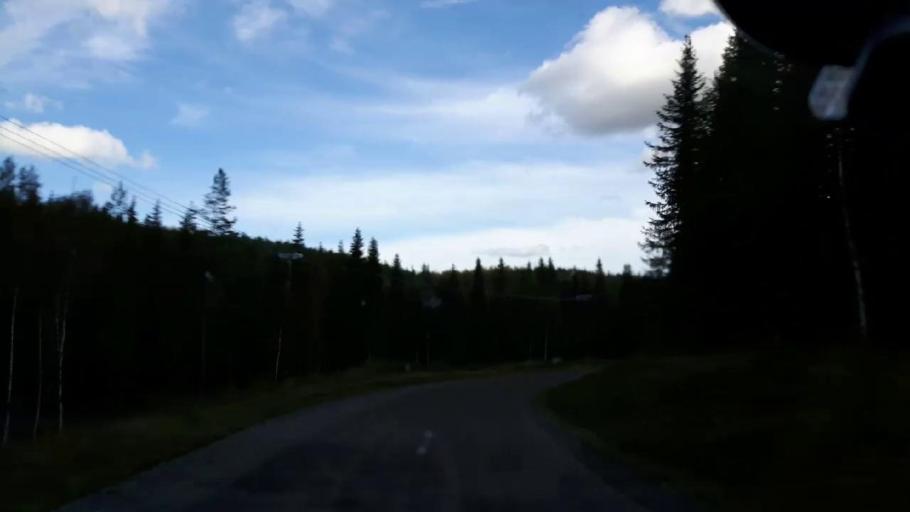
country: SE
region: Jaemtland
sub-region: Ragunda Kommun
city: Hammarstrand
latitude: 63.4213
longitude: 16.0697
